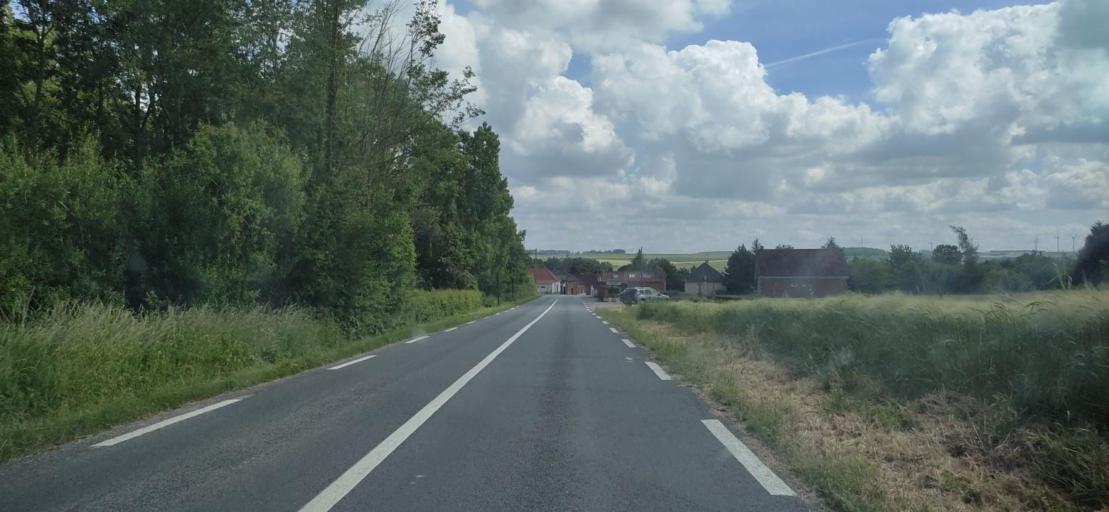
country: FR
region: Nord-Pas-de-Calais
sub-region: Departement du Pas-de-Calais
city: Therouanne
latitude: 50.6433
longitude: 2.2570
